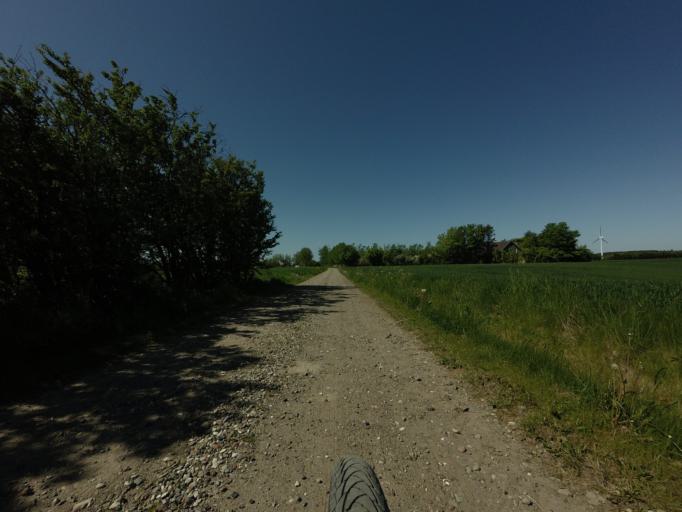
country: DK
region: North Denmark
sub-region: Hjorring Kommune
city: Hjorring
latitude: 57.4559
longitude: 9.8900
